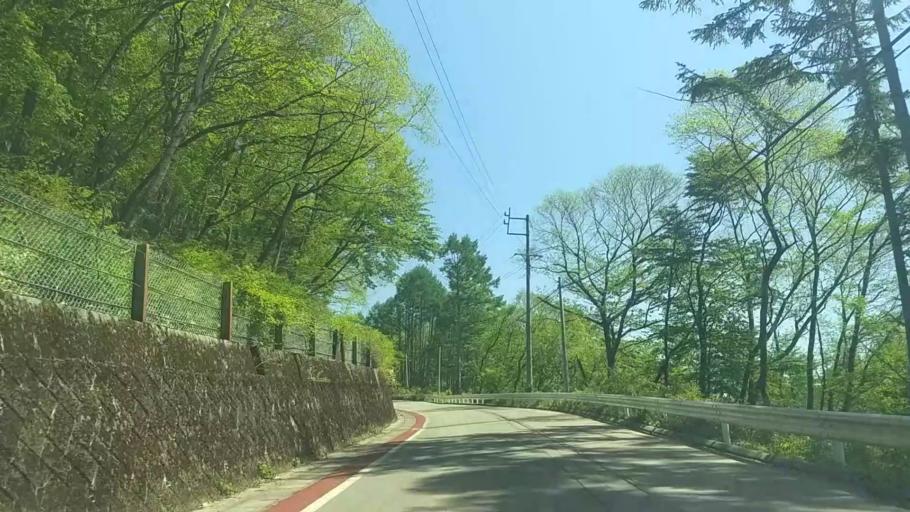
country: JP
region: Yamanashi
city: Nirasaki
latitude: 35.9199
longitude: 138.4459
